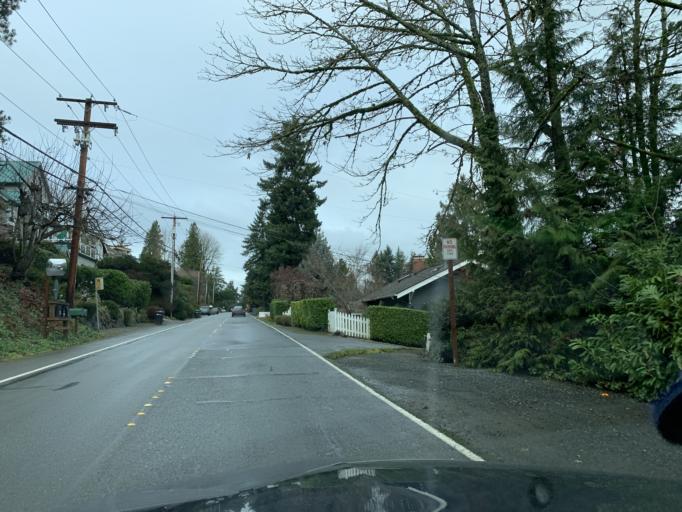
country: US
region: Washington
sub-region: King County
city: Mercer Island
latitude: 47.5923
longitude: -122.2407
